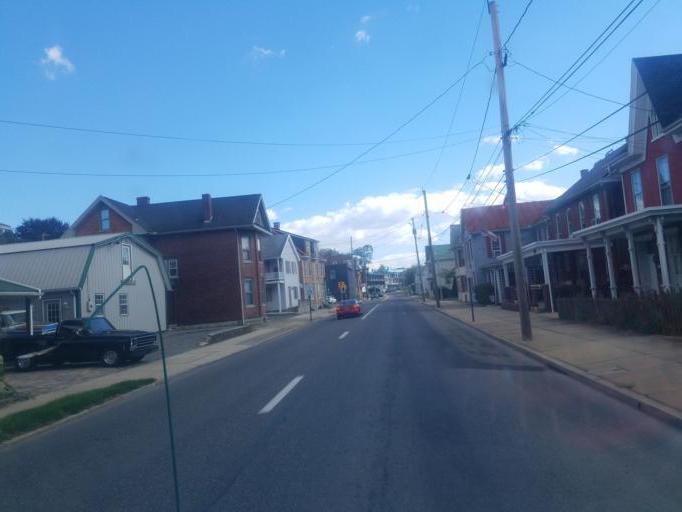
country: US
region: Pennsylvania
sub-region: Franklin County
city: Chambersburg
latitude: 39.9348
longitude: -77.6532
